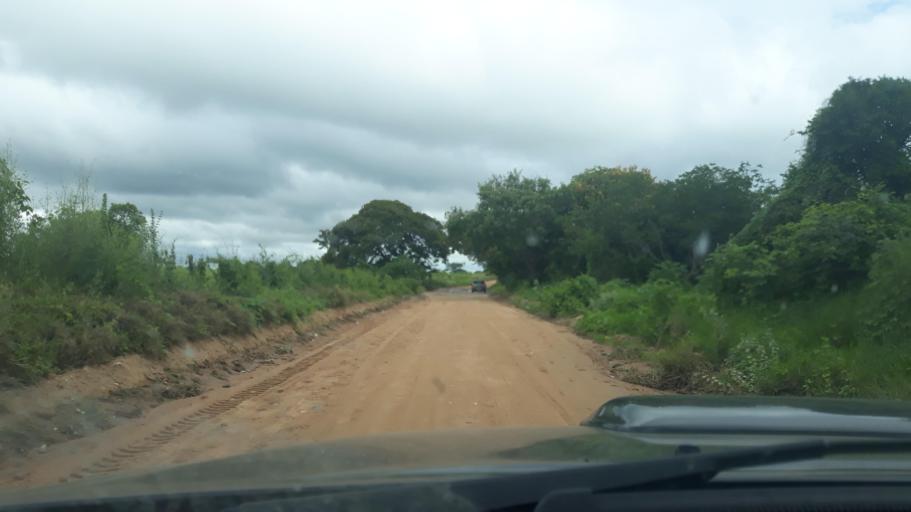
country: BR
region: Bahia
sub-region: Riacho De Santana
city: Riacho de Santana
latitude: -13.9095
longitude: -42.8511
